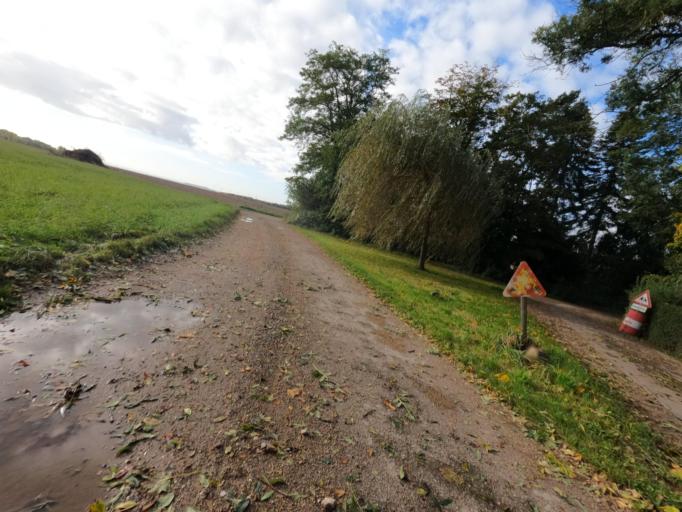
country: DE
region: North Rhine-Westphalia
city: Huckelhoven
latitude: 51.0504
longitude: 6.2728
